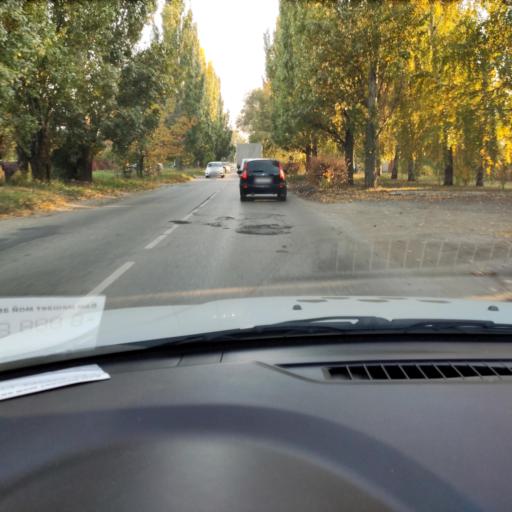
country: RU
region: Samara
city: Tol'yatti
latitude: 53.5337
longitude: 49.4180
